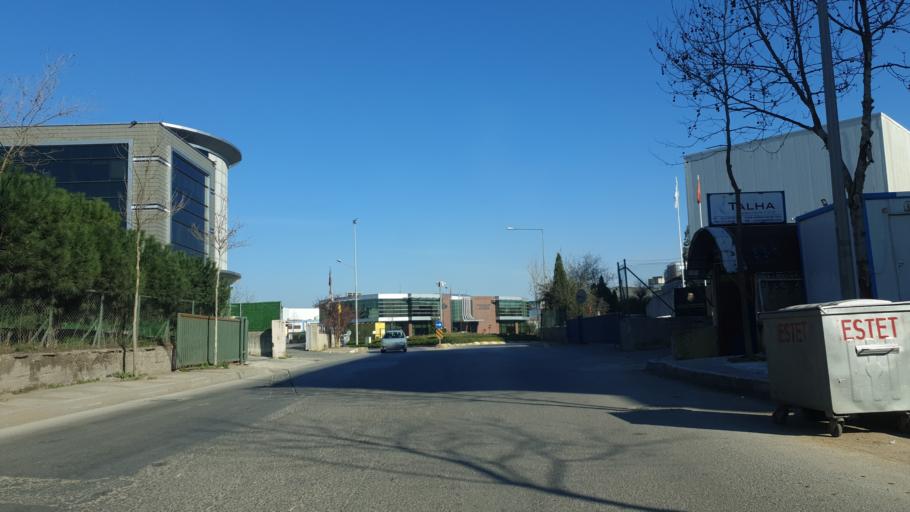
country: TR
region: Istanbul
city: Icmeler
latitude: 40.8778
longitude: 29.3639
